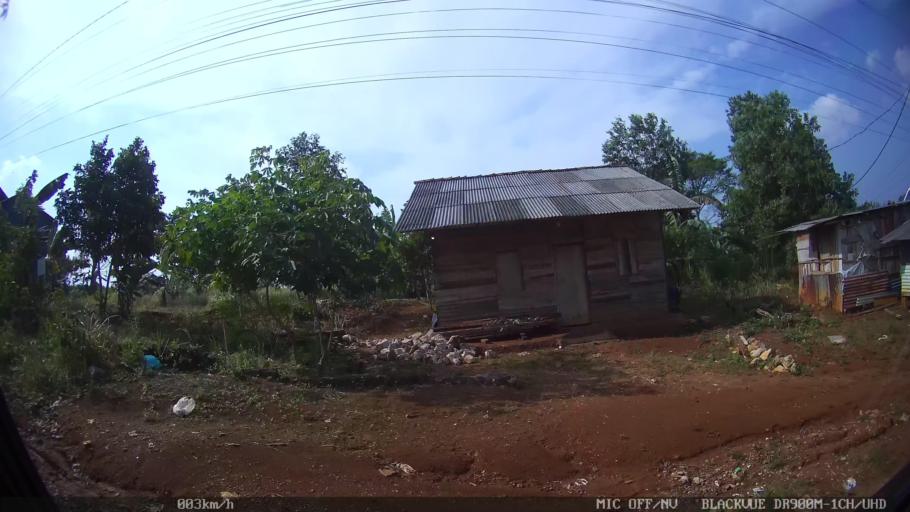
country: ID
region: Lampung
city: Kedaton
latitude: -5.3828
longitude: 105.2277
